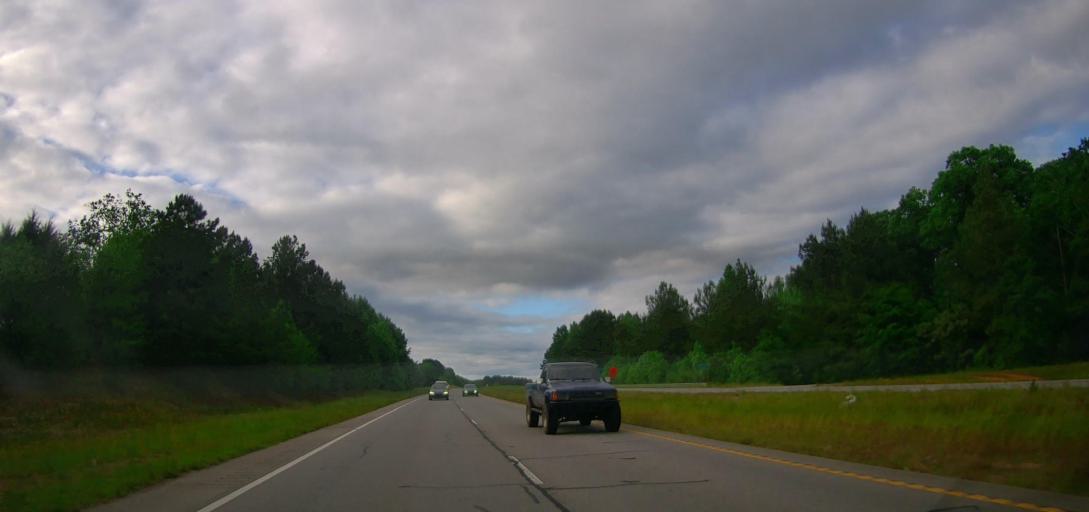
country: US
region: Georgia
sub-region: Oconee County
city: Watkinsville
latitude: 33.8629
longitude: -83.4247
